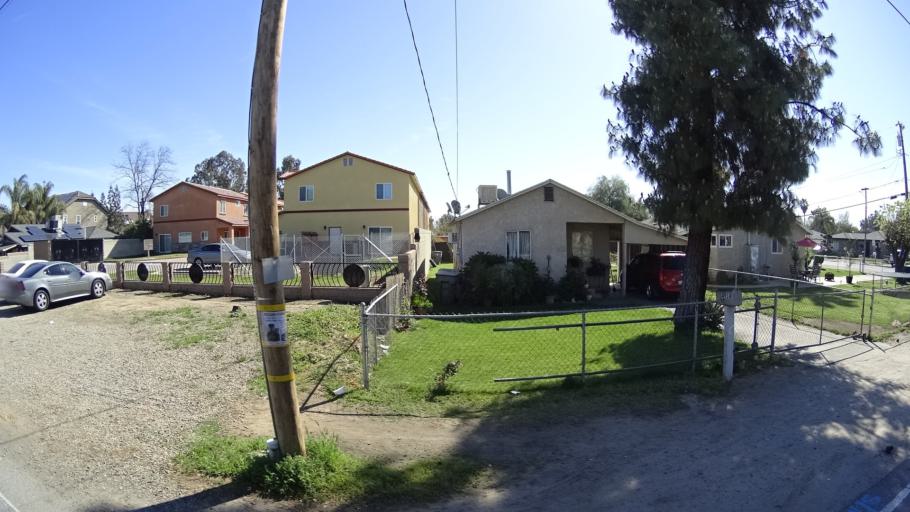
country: US
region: California
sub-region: Fresno County
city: West Park
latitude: 36.8066
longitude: -119.8895
